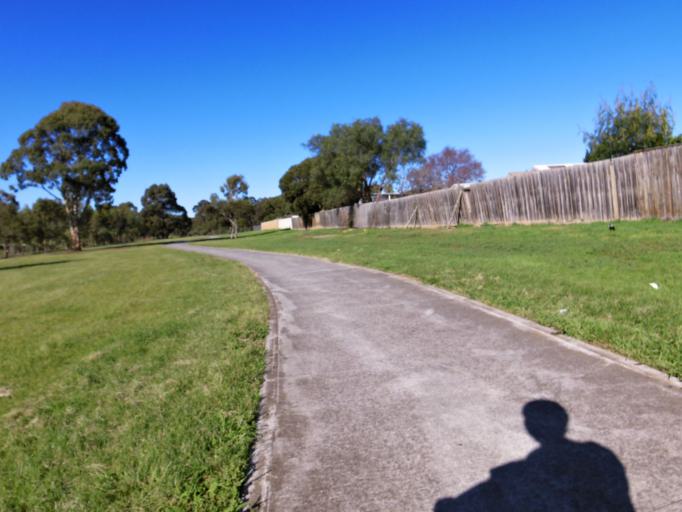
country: AU
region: Victoria
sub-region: Wyndham
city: Tarneit
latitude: -37.8795
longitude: 144.6766
